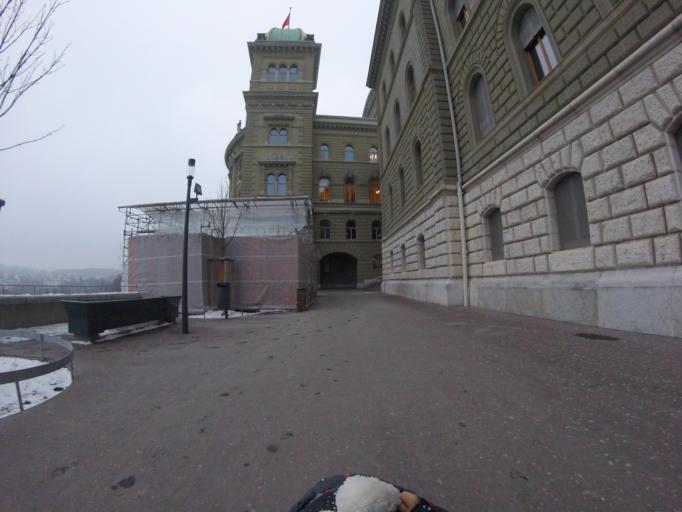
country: CH
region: Bern
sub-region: Bern-Mittelland District
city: Bern
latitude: 46.9464
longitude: 7.4451
